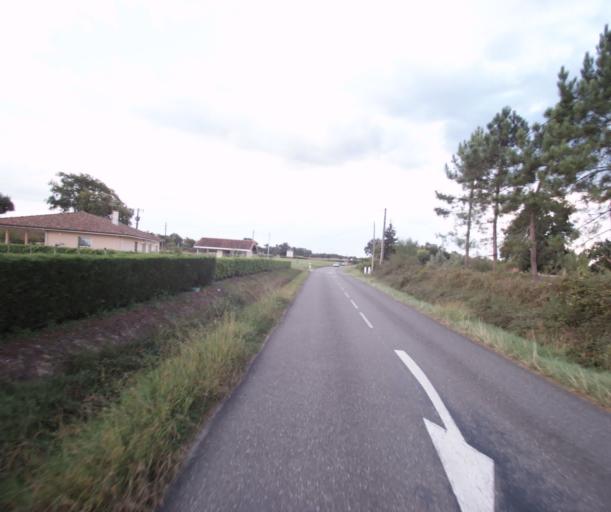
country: FR
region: Midi-Pyrenees
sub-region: Departement du Gers
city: Cazaubon
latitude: 43.9109
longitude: -0.0802
